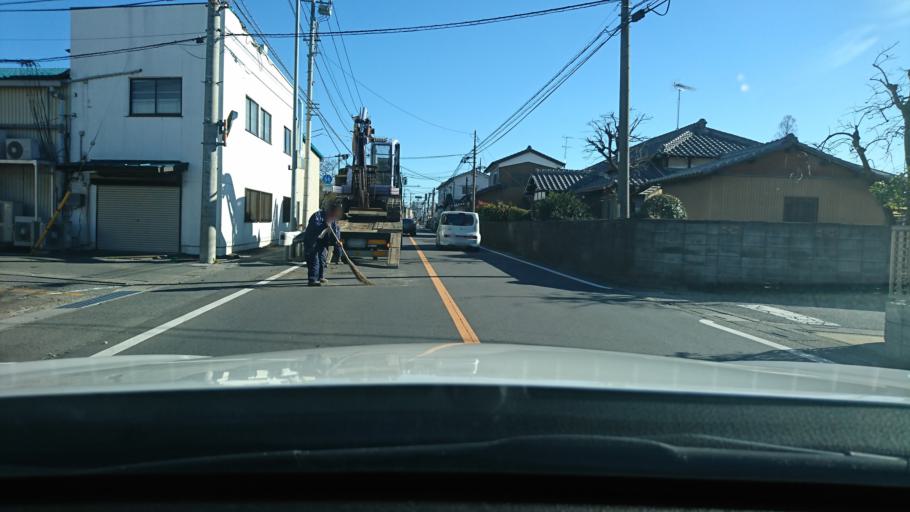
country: JP
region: Saitama
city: Yono
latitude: 35.8971
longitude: 139.5829
